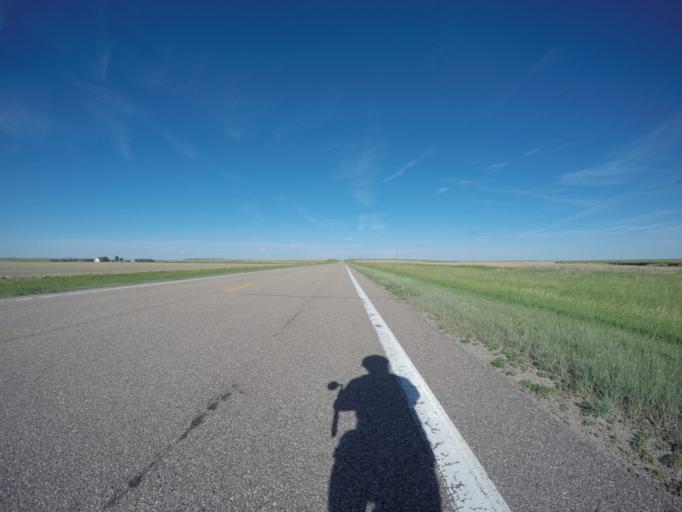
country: US
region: Kansas
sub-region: Cheyenne County
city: Saint Francis
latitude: 39.7566
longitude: -101.9596
